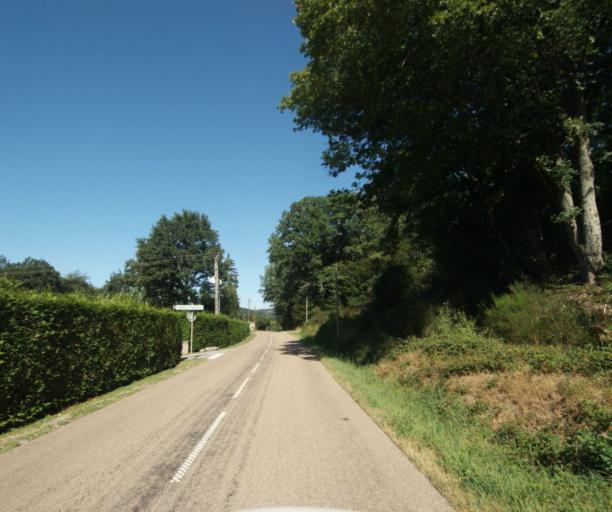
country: FR
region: Lorraine
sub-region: Departement des Vosges
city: Epinal
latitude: 48.1495
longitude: 6.4666
